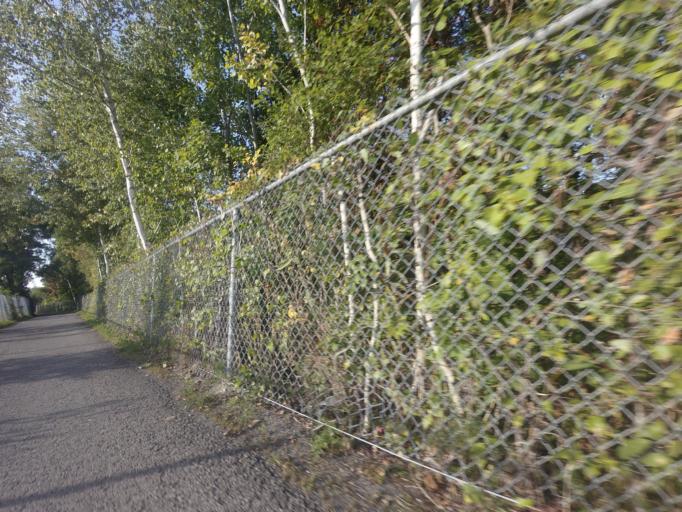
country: CA
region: Quebec
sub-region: Laurentides
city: Saint-Jerome
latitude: 45.7579
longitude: -73.9799
